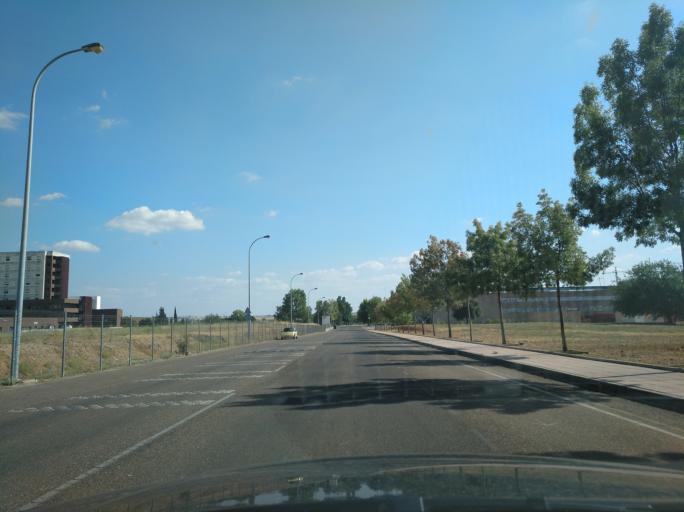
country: ES
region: Extremadura
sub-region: Provincia de Badajoz
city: Badajoz
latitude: 38.8861
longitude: -7.0034
